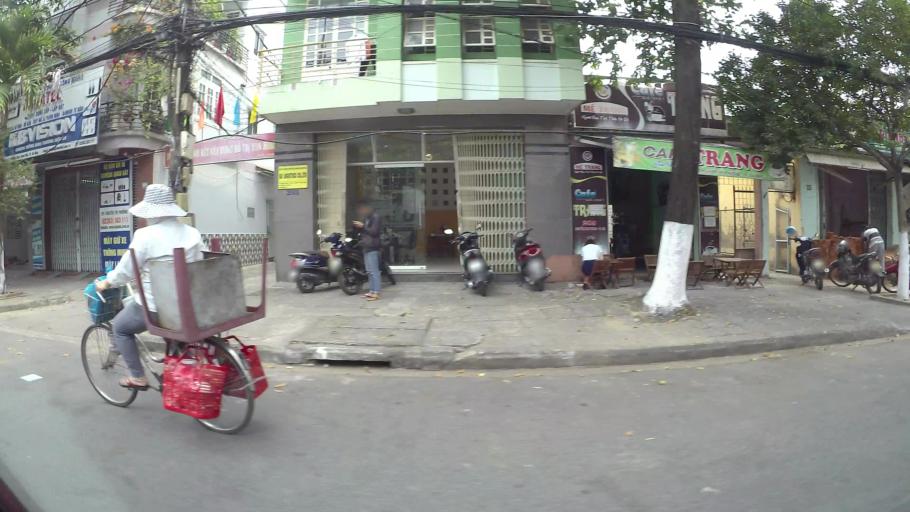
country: VN
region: Da Nang
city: Da Nang
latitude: 16.0540
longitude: 108.2099
